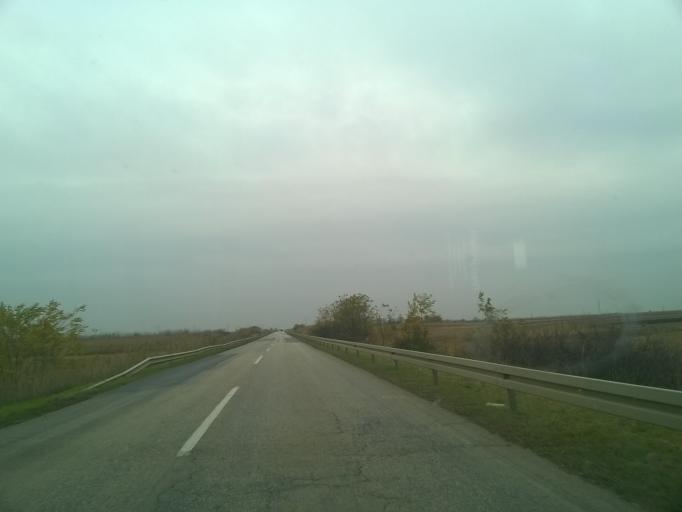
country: RS
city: Crepaja
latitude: 44.9512
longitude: 20.6633
